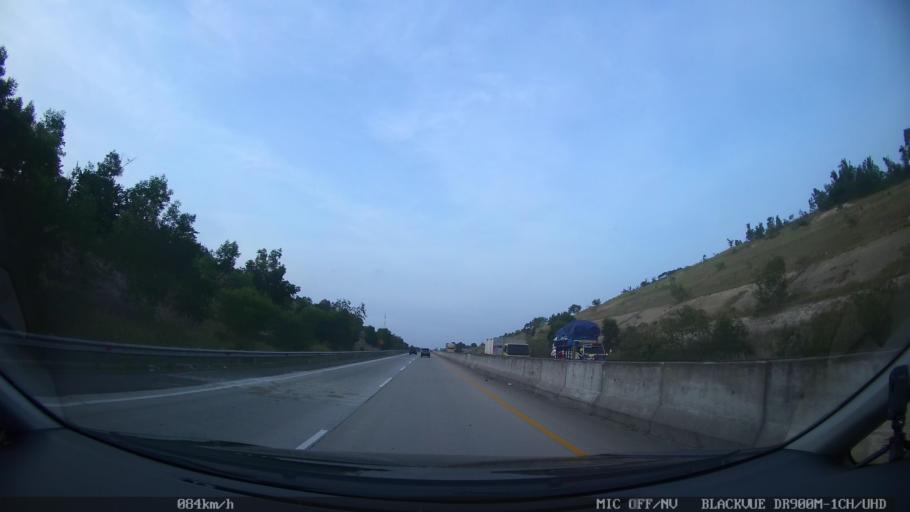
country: ID
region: Lampung
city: Penengahan
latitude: -5.8279
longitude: 105.7329
